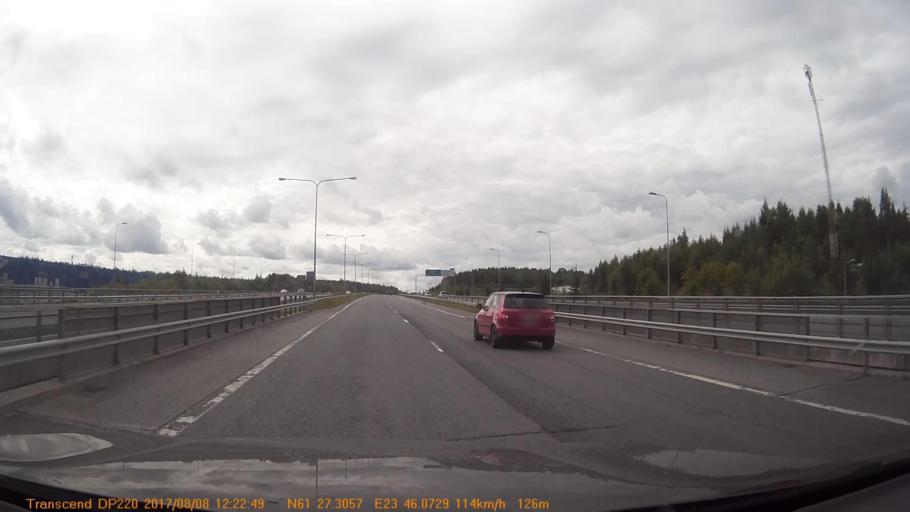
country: FI
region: Pirkanmaa
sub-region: Tampere
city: Tampere
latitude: 61.4547
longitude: 23.7678
